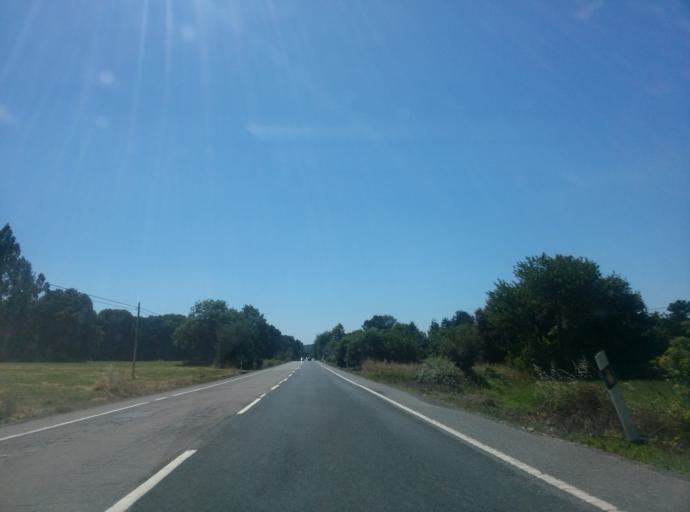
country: ES
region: Galicia
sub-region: Provincia de Lugo
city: Castro de Rei
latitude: 43.1171
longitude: -7.4389
